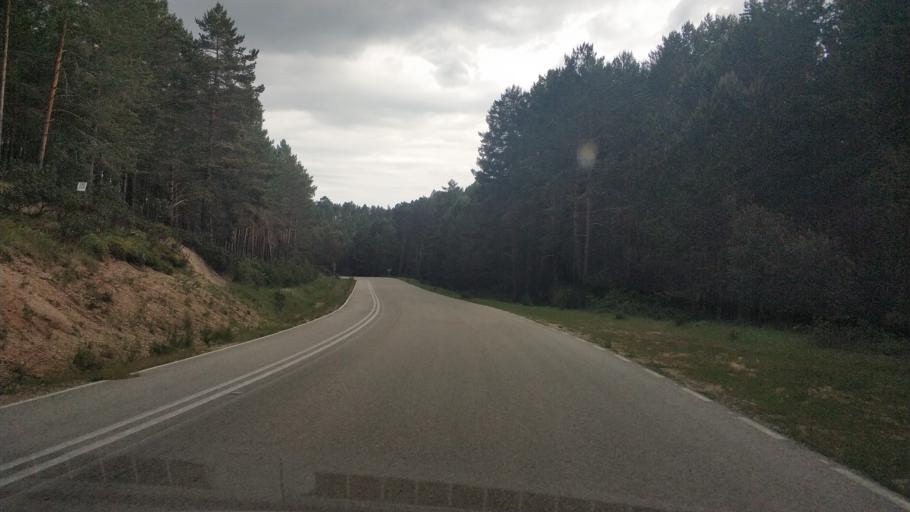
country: ES
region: Castille and Leon
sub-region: Provincia de Soria
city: San Leonardo de Yague
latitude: 41.8504
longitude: -3.0696
